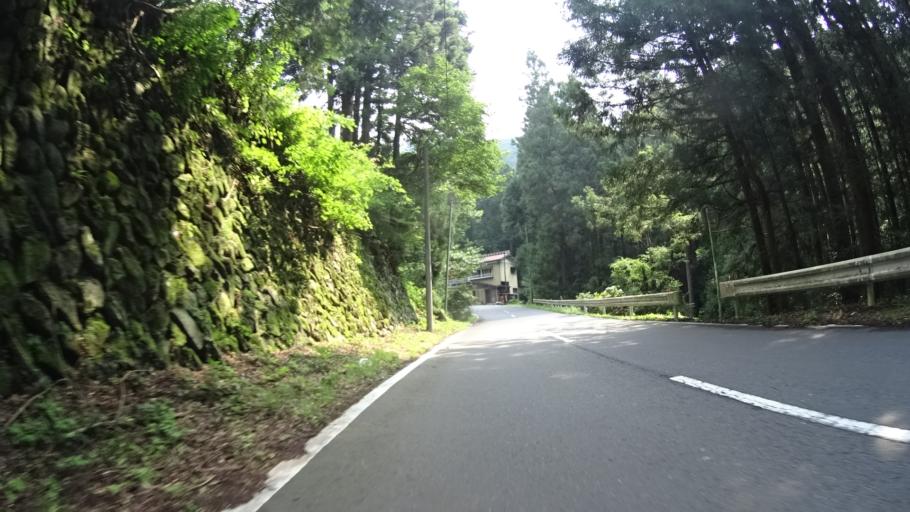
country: JP
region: Gunma
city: Tomioka
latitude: 36.0614
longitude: 138.8599
